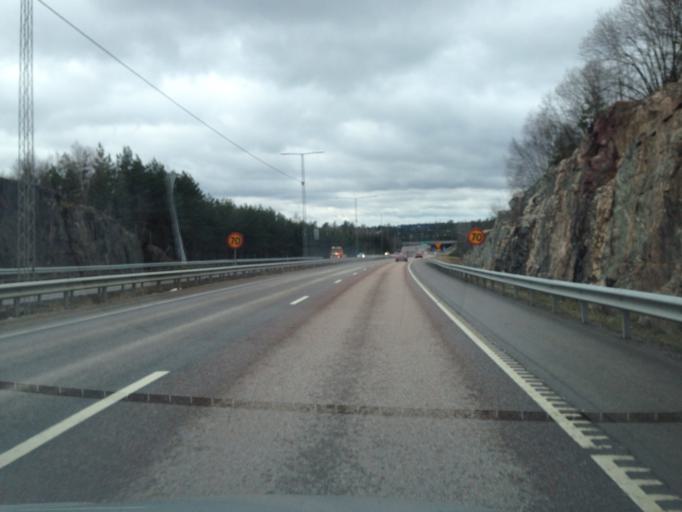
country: SE
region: Stockholm
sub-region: Vallentuna Kommun
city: Vallentuna
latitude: 59.4952
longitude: 18.1725
